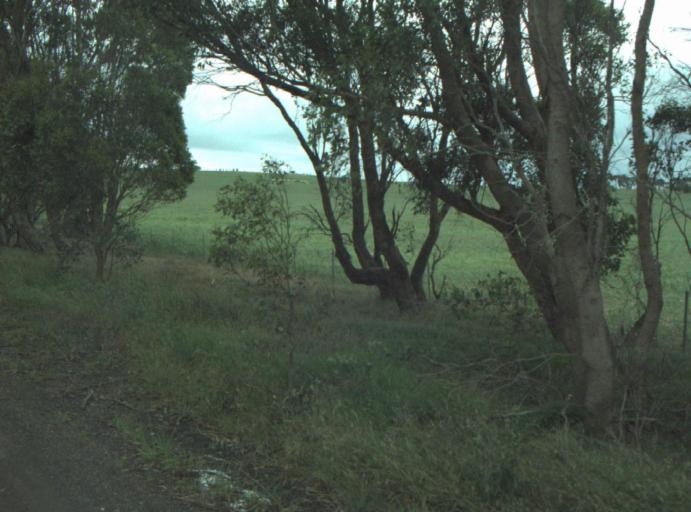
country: AU
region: Victoria
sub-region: Greater Geelong
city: Lara
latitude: -37.8824
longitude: 144.3502
